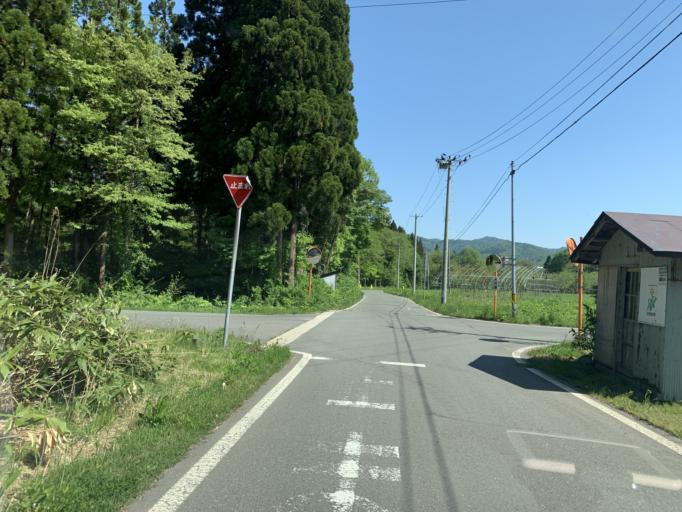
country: JP
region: Iwate
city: Shizukuishi
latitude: 39.5627
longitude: 140.8387
